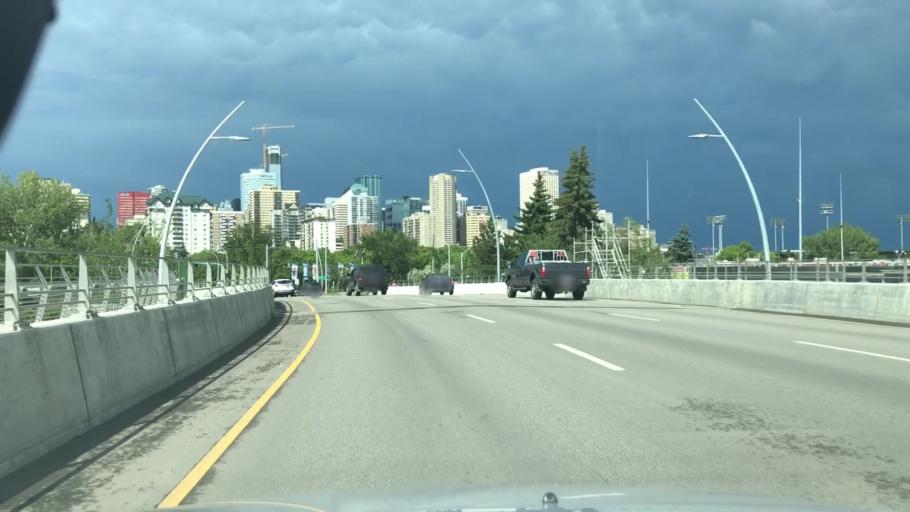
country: CA
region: Alberta
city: Edmonton
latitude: 53.5292
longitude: -113.5013
